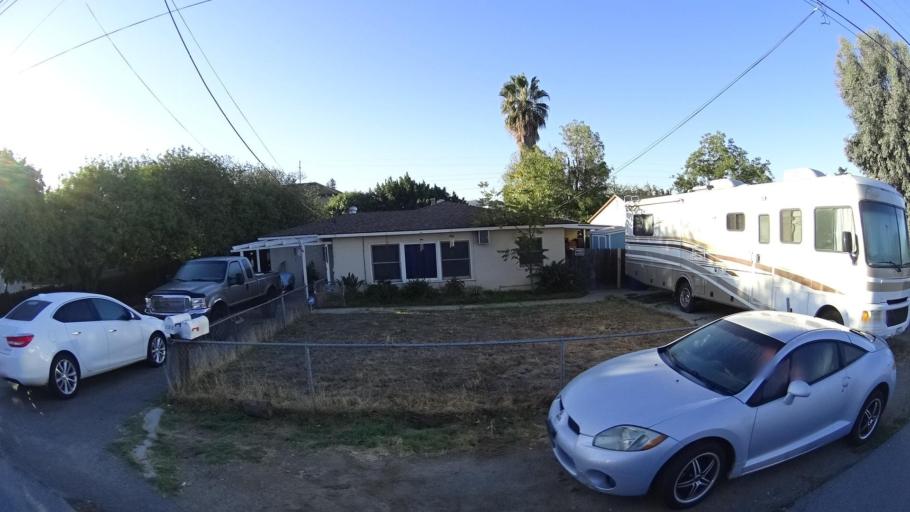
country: US
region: California
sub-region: San Diego County
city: Bostonia
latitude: 32.8090
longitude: -116.9469
